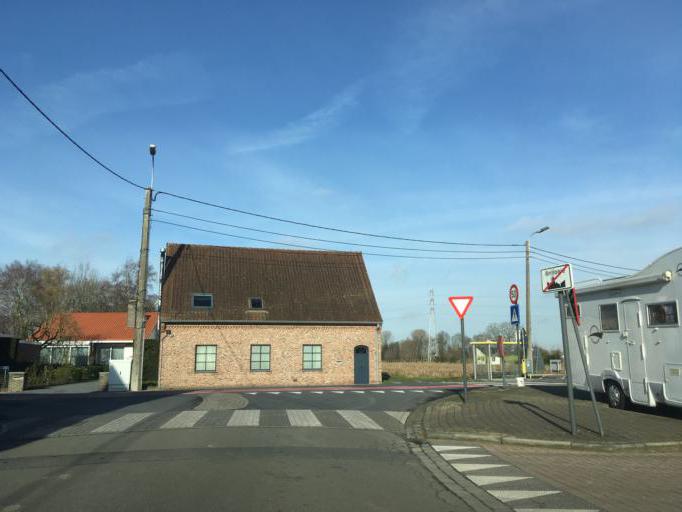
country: BE
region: Flanders
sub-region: Provincie West-Vlaanderen
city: Ardooie
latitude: 50.9589
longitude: 3.1683
